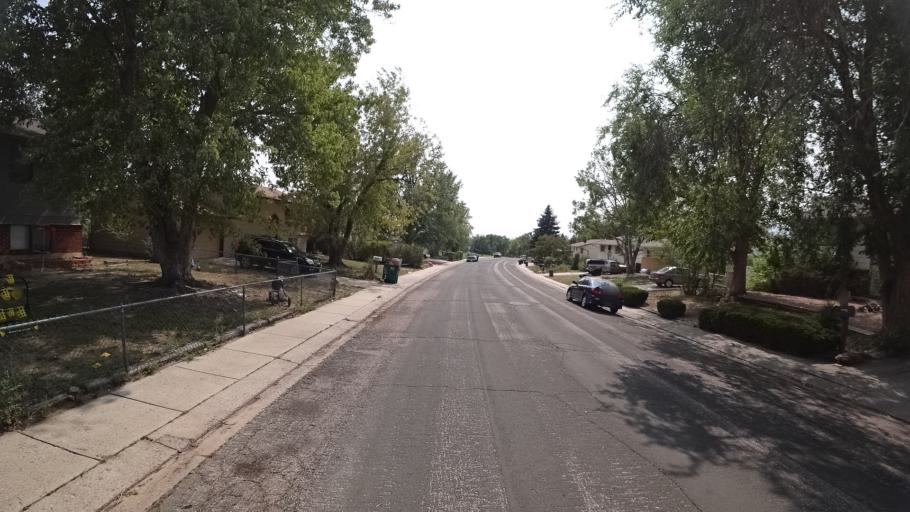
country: US
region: Colorado
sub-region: El Paso County
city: Stratmoor
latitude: 38.8023
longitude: -104.7675
